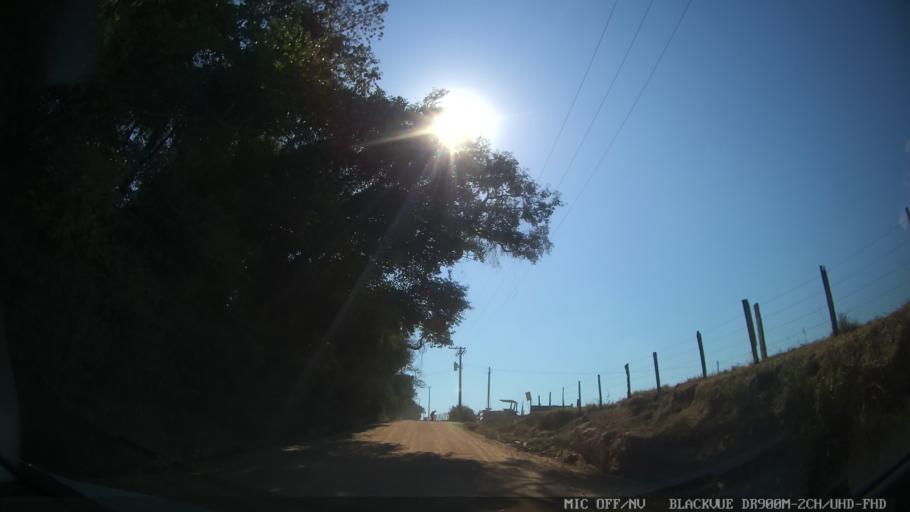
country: BR
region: Sao Paulo
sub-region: Itupeva
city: Itupeva
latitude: -23.1016
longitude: -47.0853
